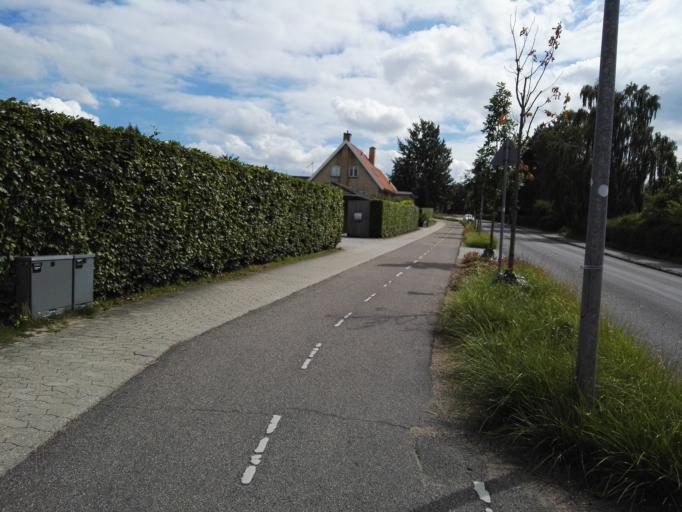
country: DK
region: Capital Region
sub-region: Ballerup Kommune
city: Malov
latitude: 55.7587
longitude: 12.3389
